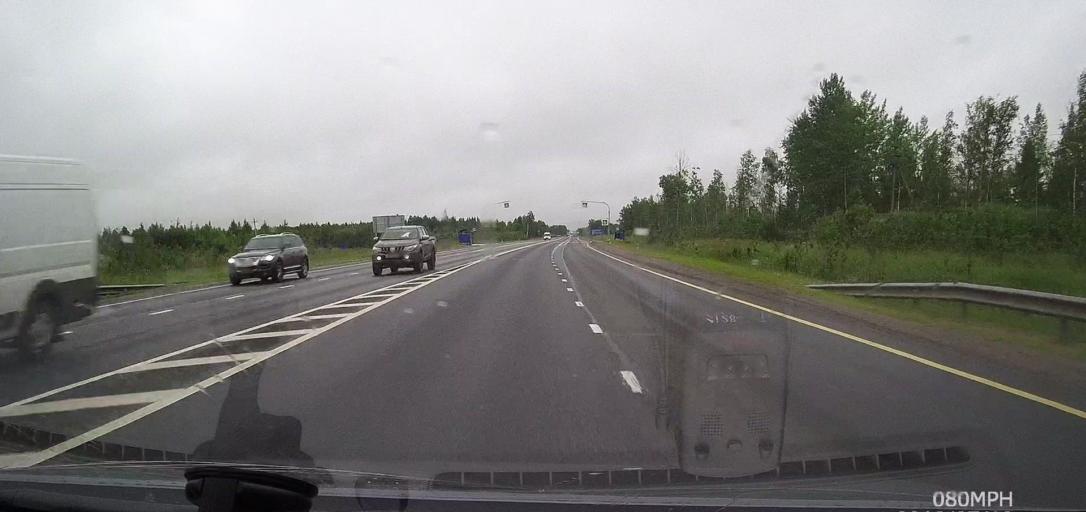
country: RU
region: Leningrad
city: Staraya Ladoga
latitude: 59.9977
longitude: 32.1043
